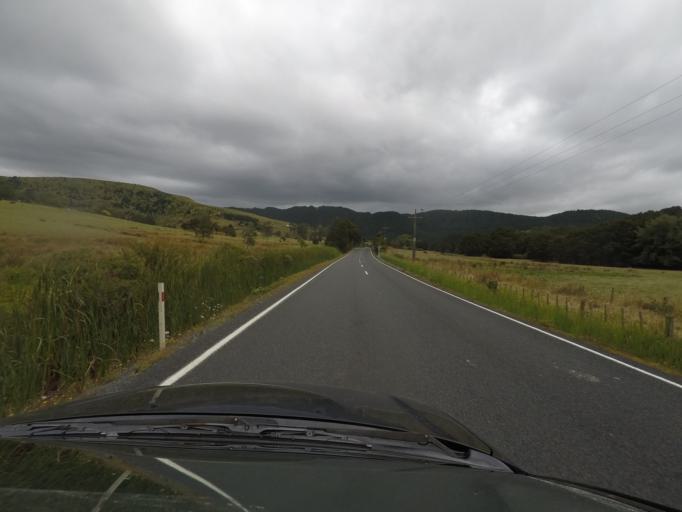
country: NZ
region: Auckland
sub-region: Auckland
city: Wellsford
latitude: -36.2895
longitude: 174.6277
